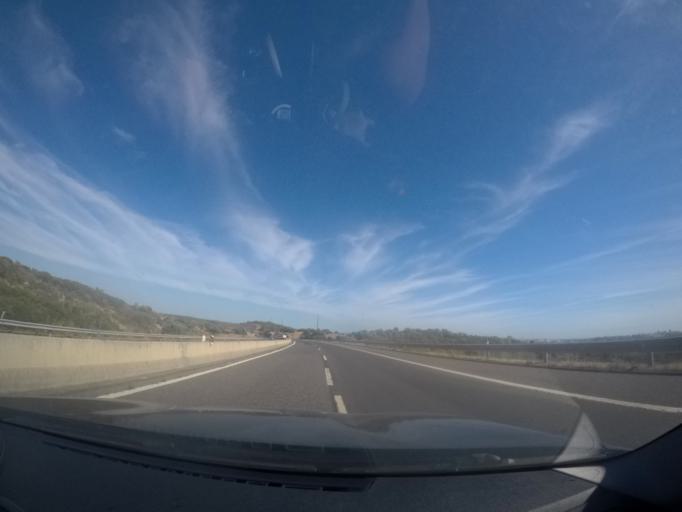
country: PT
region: Faro
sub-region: Lagoa
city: Estombar
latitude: 37.1661
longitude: -8.5125
